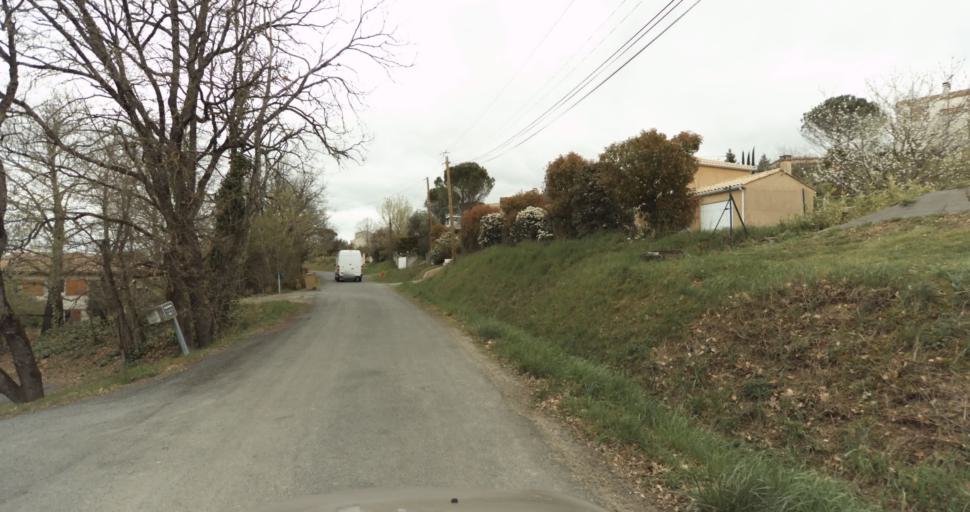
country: FR
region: Midi-Pyrenees
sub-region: Departement du Tarn
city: Puygouzon
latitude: 43.9043
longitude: 2.1614
